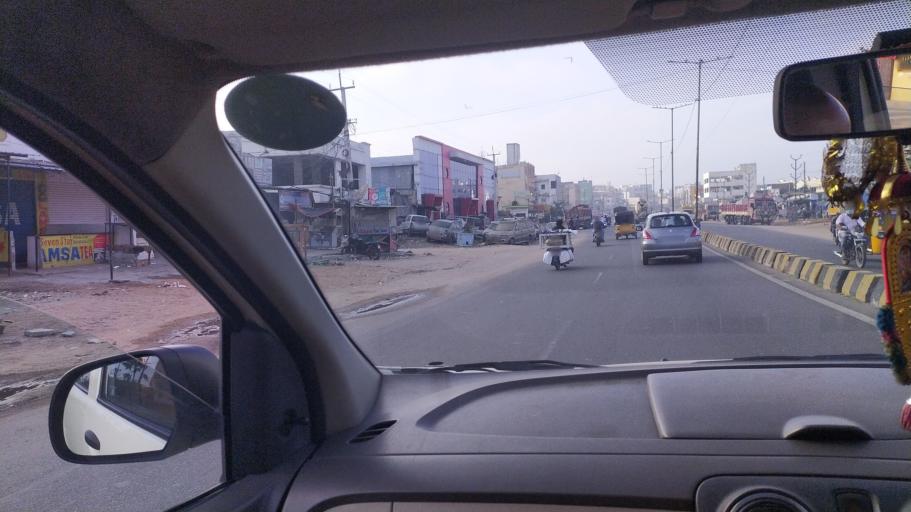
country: IN
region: Telangana
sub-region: Rangareddi
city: Balapur
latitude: 17.3206
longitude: 78.4674
